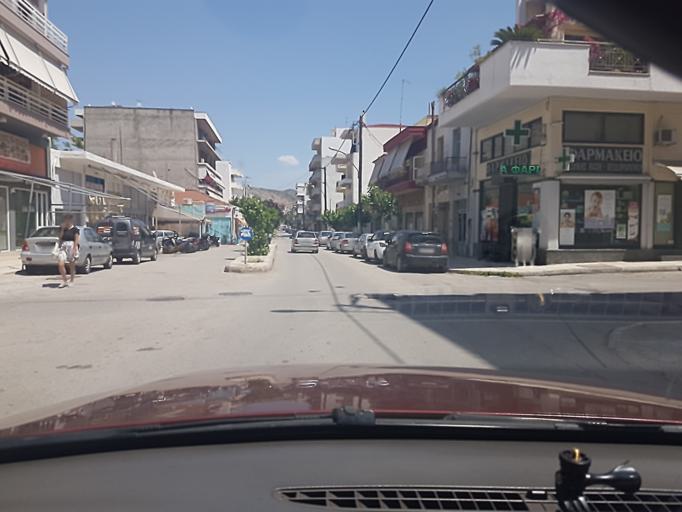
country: GR
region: Central Greece
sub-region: Nomos Evvoias
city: Chalkida
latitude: 38.4620
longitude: 23.6006
